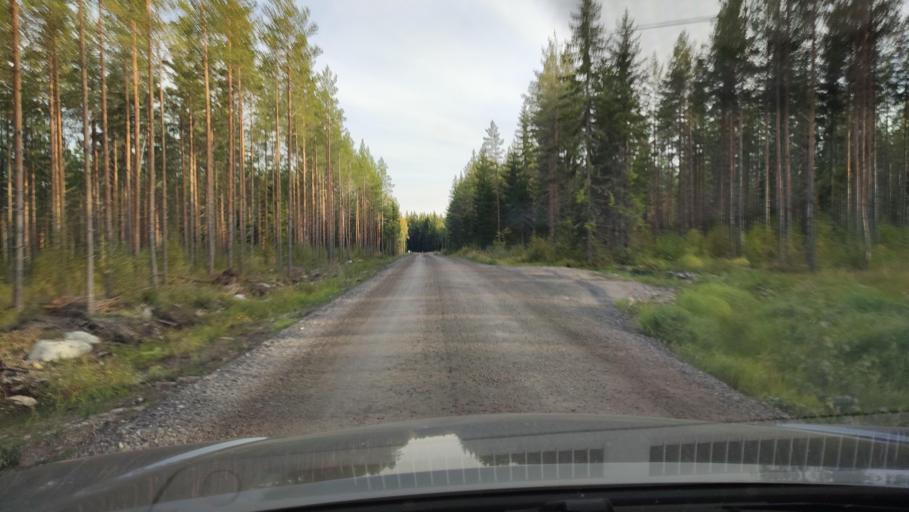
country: FI
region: Southern Ostrobothnia
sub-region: Suupohja
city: Karijoki
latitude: 62.1702
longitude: 21.5939
